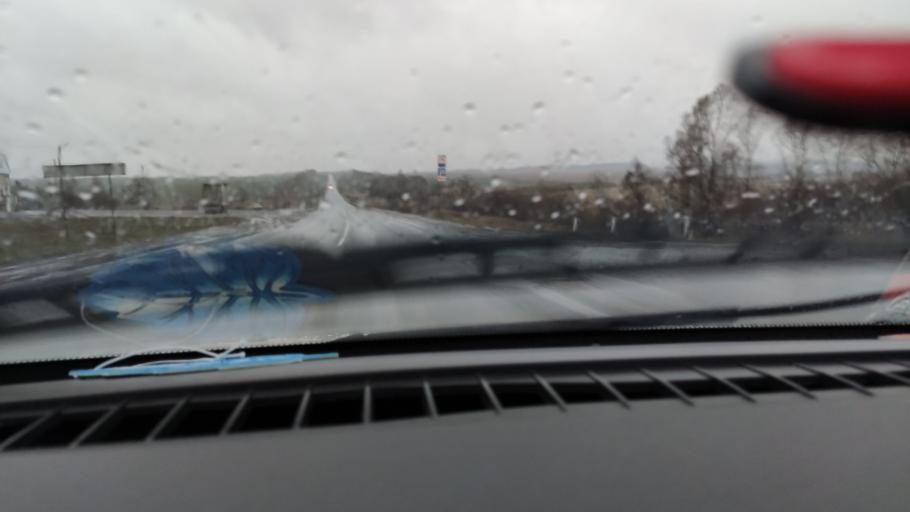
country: RU
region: Tatarstan
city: Mendeleyevsk
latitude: 55.9391
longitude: 52.2894
